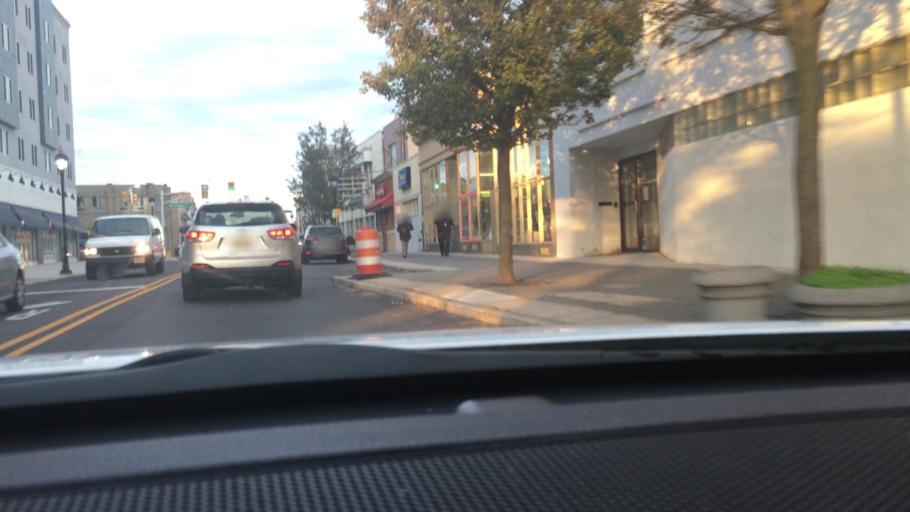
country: US
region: New Jersey
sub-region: Atlantic County
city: Pleasantville
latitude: 39.3912
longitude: -74.5230
